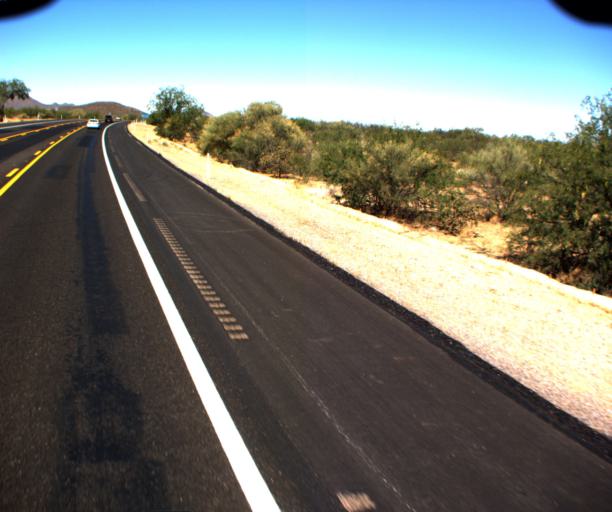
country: US
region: Arizona
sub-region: Pima County
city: Sells
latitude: 31.9319
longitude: -111.7803
